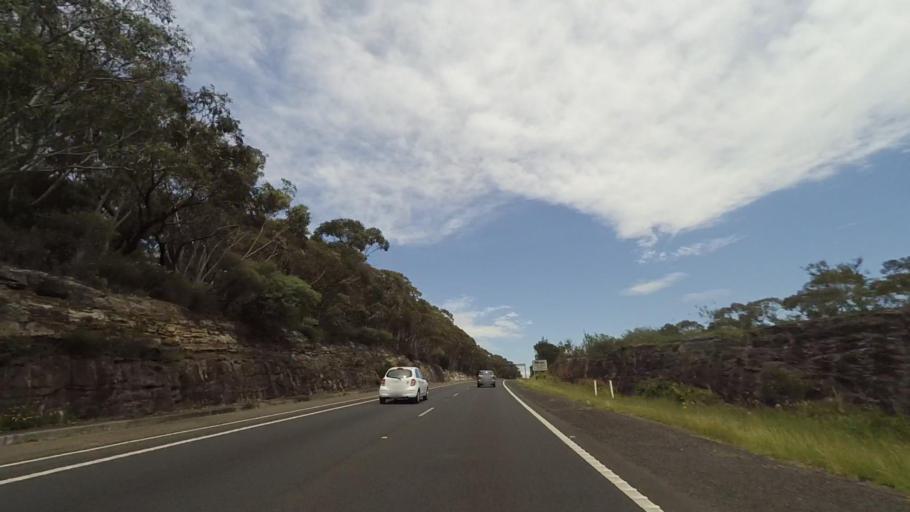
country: AU
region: New South Wales
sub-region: Wollongong
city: Helensburgh
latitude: -34.2432
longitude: 150.9428
